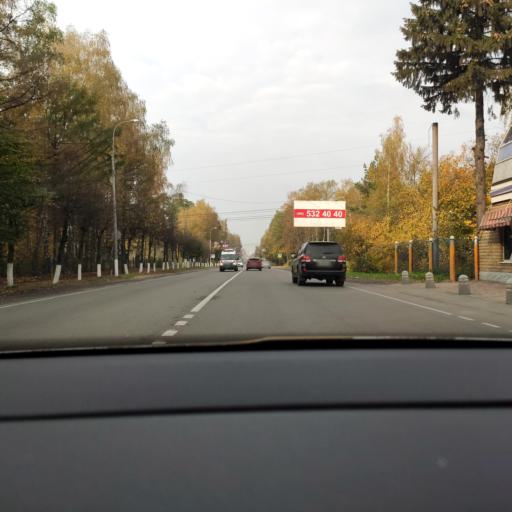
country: RU
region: Moskovskaya
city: Lesnyye Polyany
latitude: 55.9810
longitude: 37.8924
